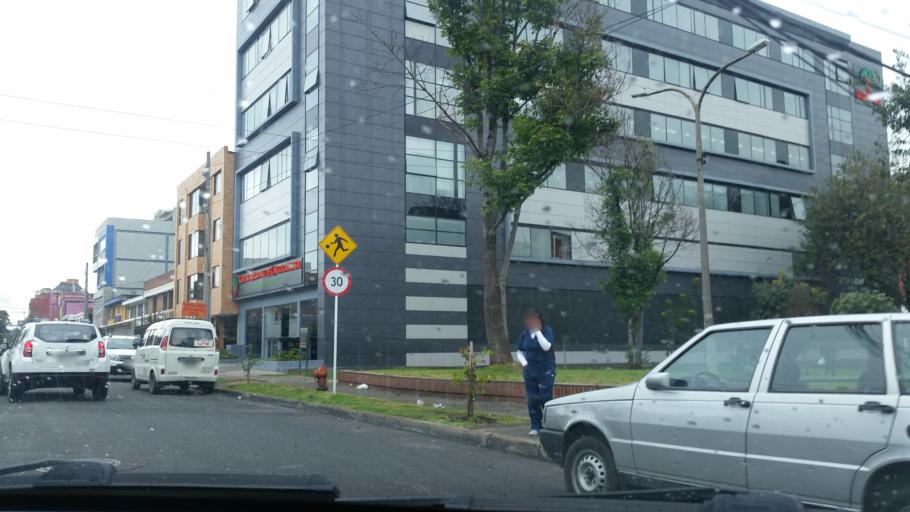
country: CO
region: Bogota D.C.
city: Barrio San Luis
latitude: 4.6820
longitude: -74.0601
